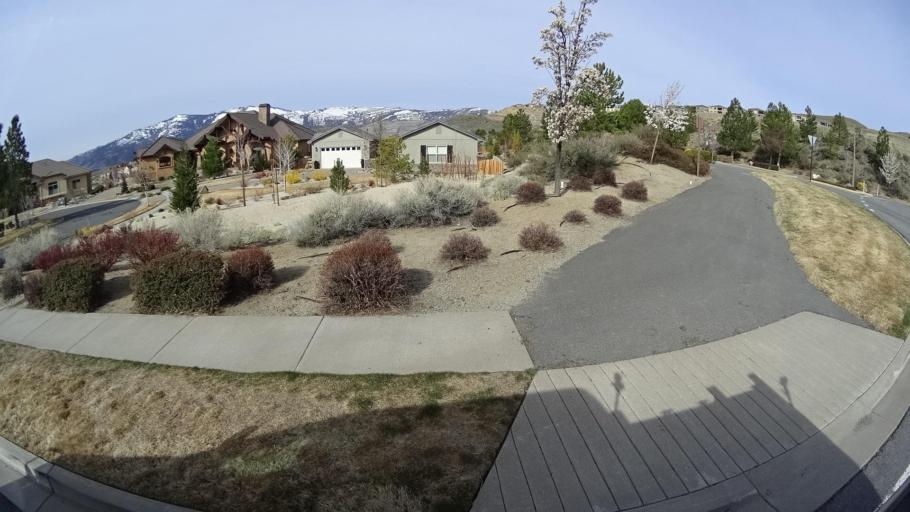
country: US
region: Nevada
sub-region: Washoe County
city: Mogul
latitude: 39.5360
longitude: -119.9453
